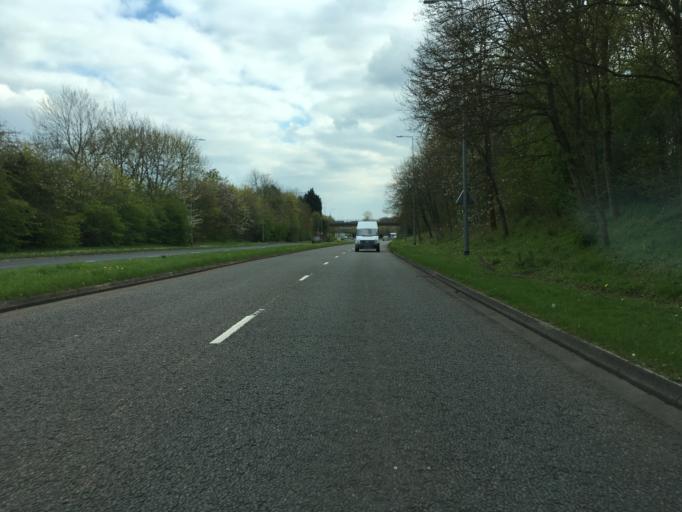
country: GB
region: England
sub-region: Milton Keynes
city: Milton Keynes
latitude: 52.0487
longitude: -0.7660
